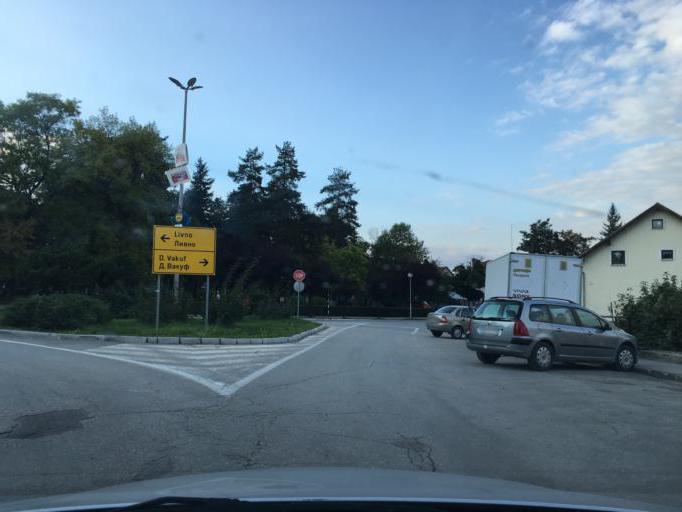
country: BA
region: Federation of Bosnia and Herzegovina
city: Bugojno
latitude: 44.0569
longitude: 17.4492
